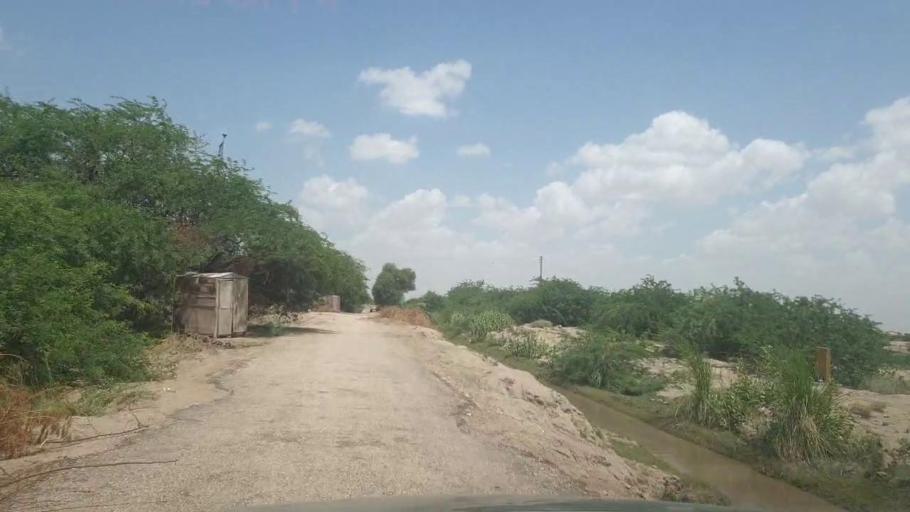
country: PK
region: Sindh
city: Kot Diji
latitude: 27.2354
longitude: 69.0222
